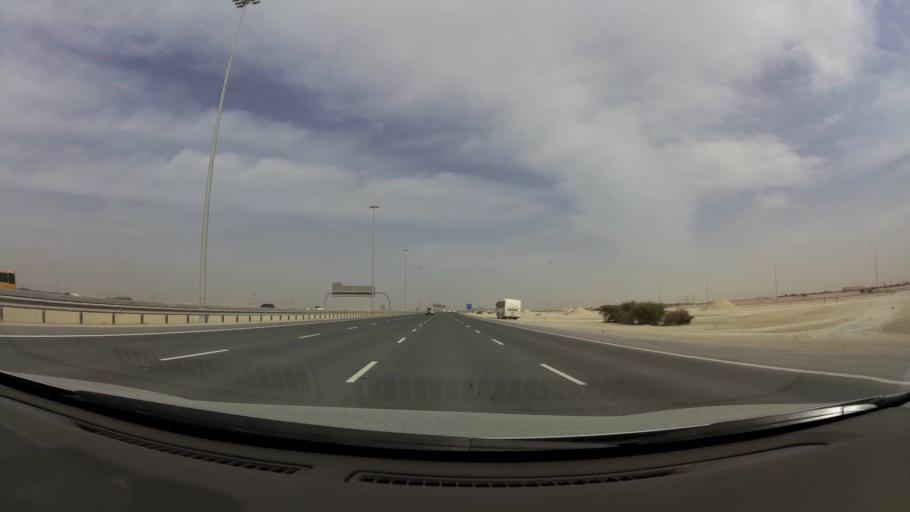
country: QA
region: Baladiyat ar Rayyan
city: Ash Shahaniyah
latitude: 25.3529
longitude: 51.2868
